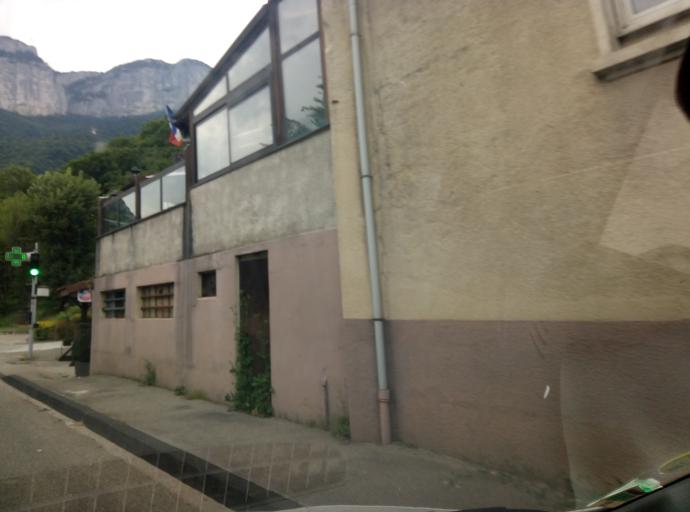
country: FR
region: Rhone-Alpes
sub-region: Departement de l'Isere
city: Noyarey
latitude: 45.2436
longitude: 5.6323
